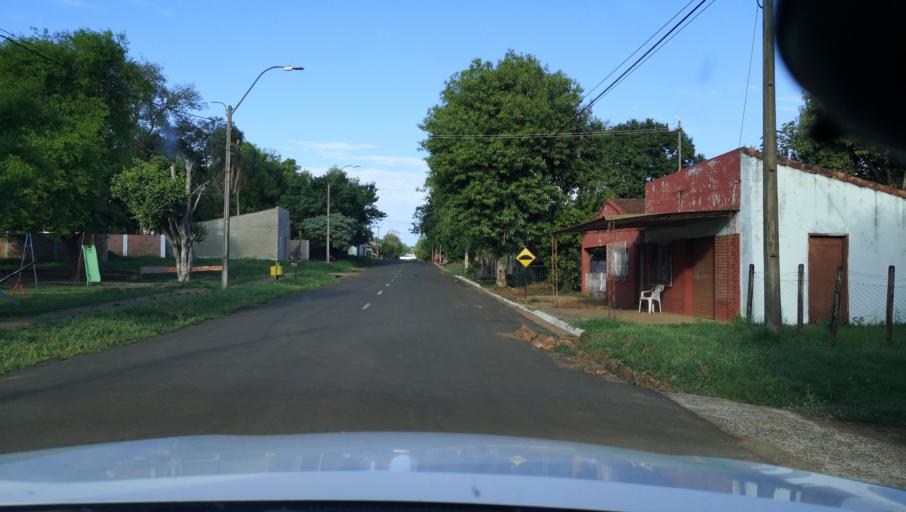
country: PY
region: Itapua
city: Carmen del Parana
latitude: -27.1599
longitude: -56.2344
